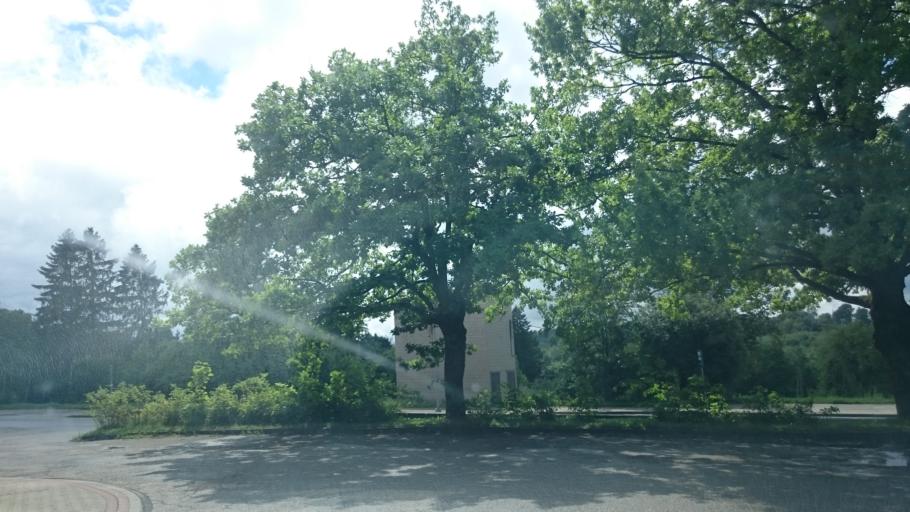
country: LV
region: Aizpute
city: Aizpute
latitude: 56.7074
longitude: 21.6225
